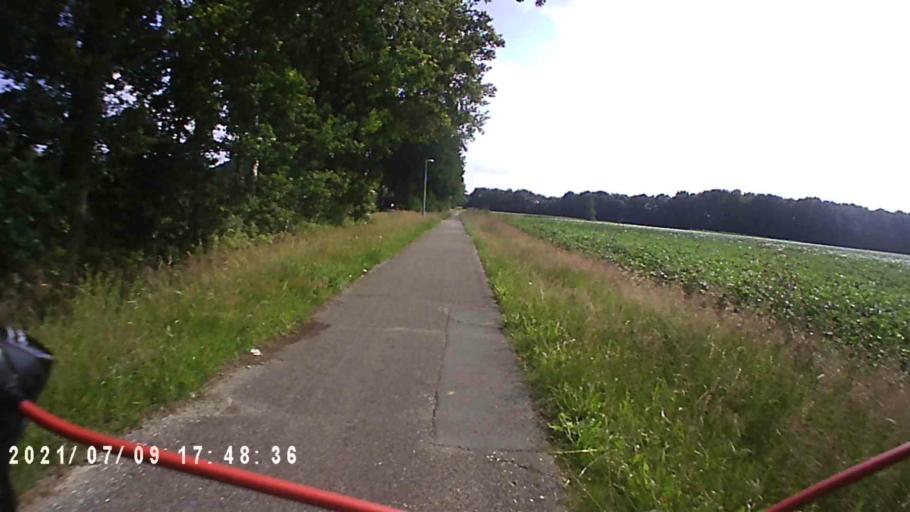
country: NL
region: Groningen
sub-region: Gemeente Vlagtwedde
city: Vlagtwedde
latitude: 53.0780
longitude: 7.0777
